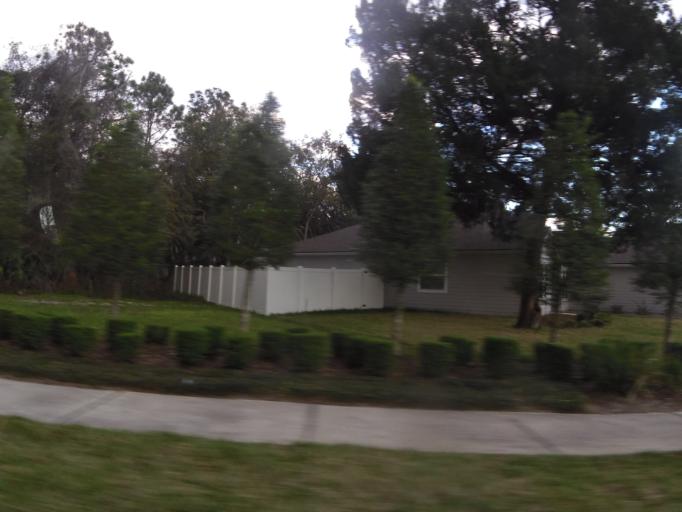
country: US
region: Florida
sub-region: Saint Johns County
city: Fruit Cove
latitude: 30.1721
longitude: -81.5681
